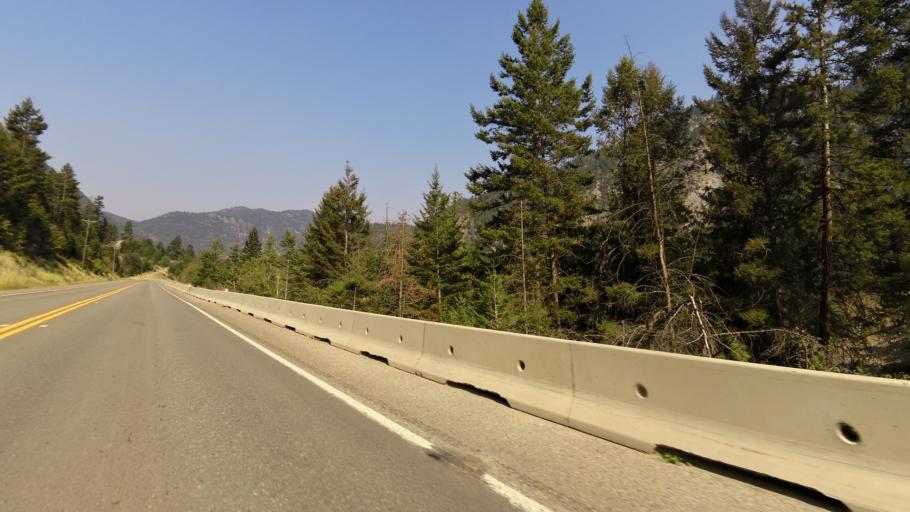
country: CA
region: British Columbia
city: Princeton
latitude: 49.3990
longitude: -120.2256
